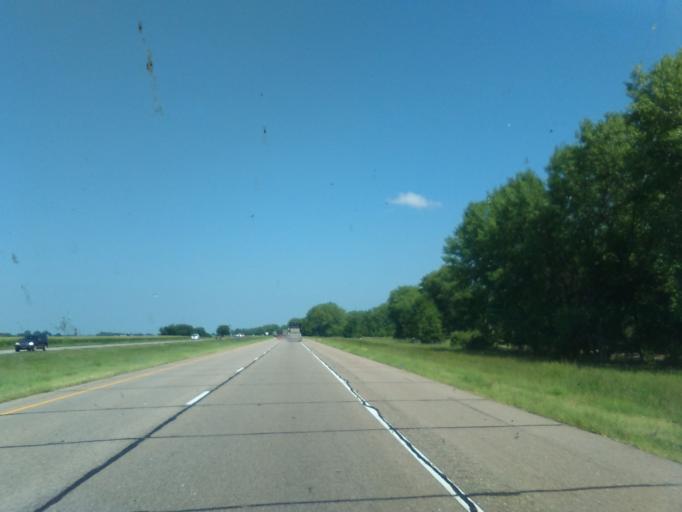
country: US
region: Nebraska
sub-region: Buffalo County
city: Kearney
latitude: 40.6727
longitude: -99.2242
